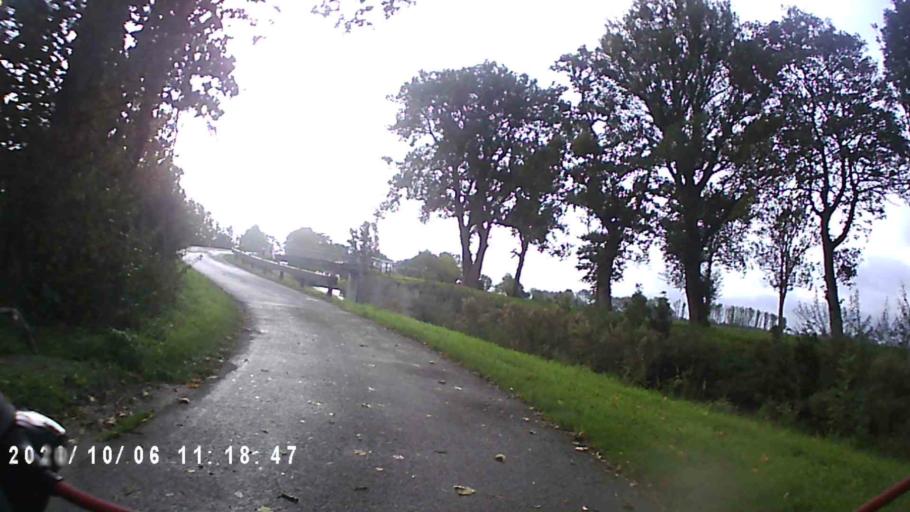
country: NL
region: Groningen
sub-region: Gemeente Zuidhorn
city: Oldehove
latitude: 53.3508
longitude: 6.3917
